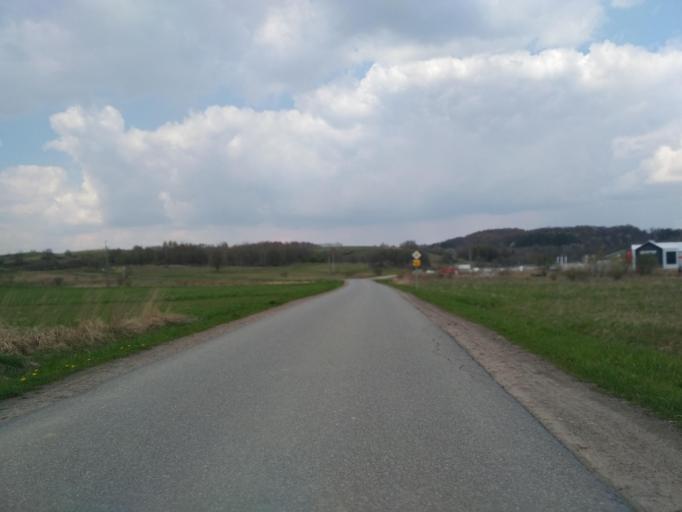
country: PL
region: Subcarpathian Voivodeship
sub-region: Powiat sanocki
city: Strachocina
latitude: 49.6136
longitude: 22.0744
